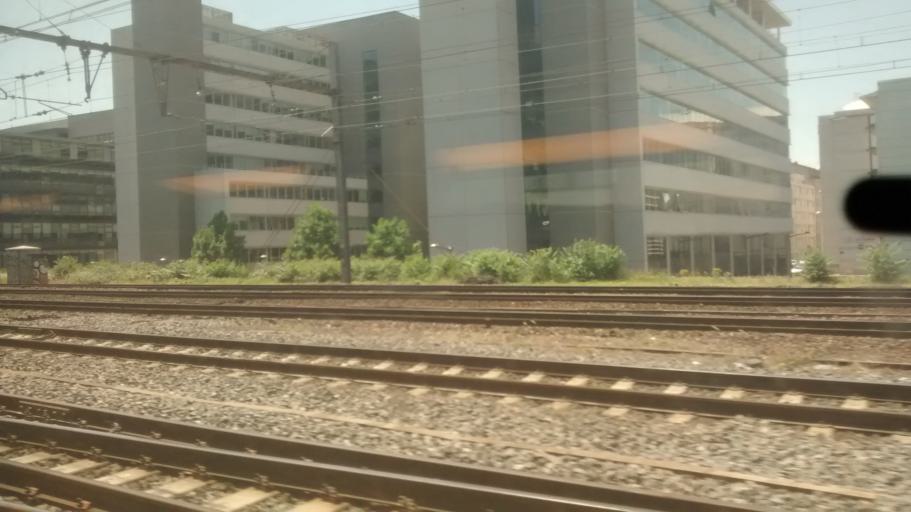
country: FR
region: Rhone-Alpes
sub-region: Departement du Rhone
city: Lyon
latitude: 45.7548
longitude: 4.8606
